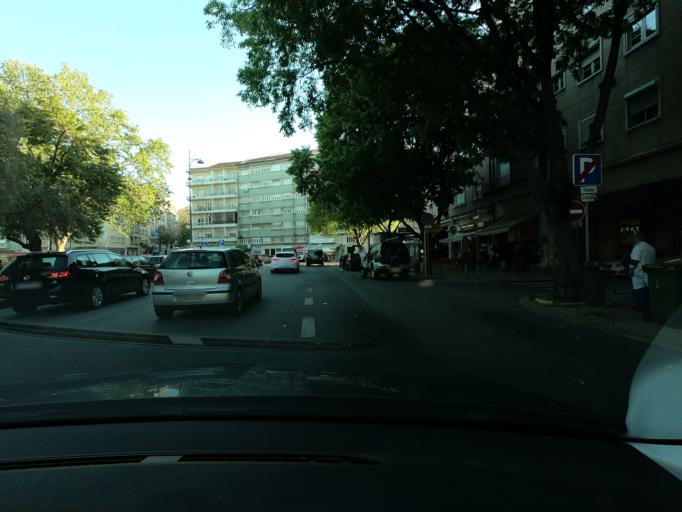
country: PT
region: Lisbon
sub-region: Lisbon
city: Lisbon
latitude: 38.7314
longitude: -9.1278
